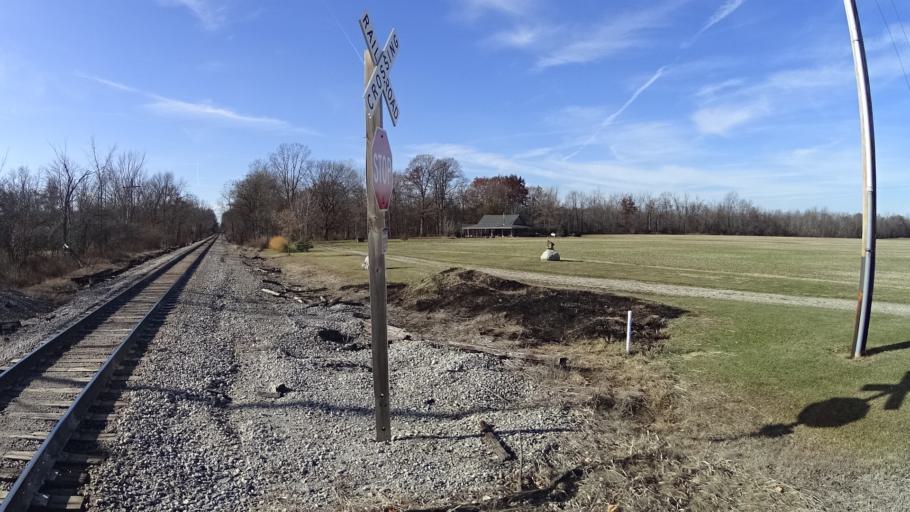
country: US
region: Ohio
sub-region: Lorain County
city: Wellington
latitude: 41.0930
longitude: -82.2009
